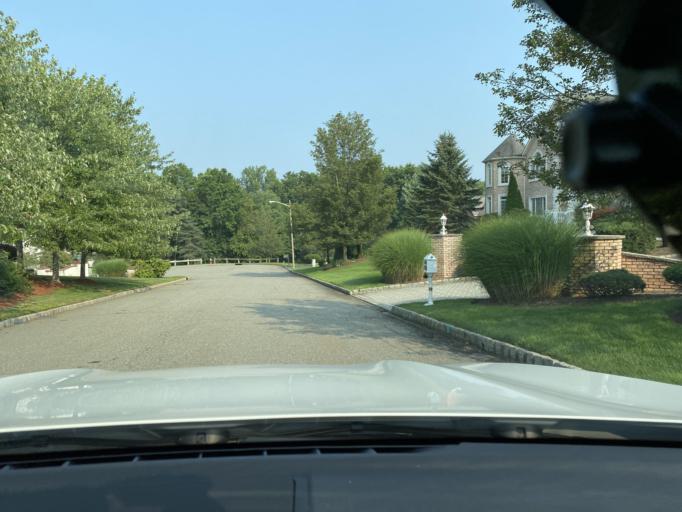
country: US
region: New York
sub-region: Rockland County
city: Airmont
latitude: 41.0843
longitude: -74.1248
